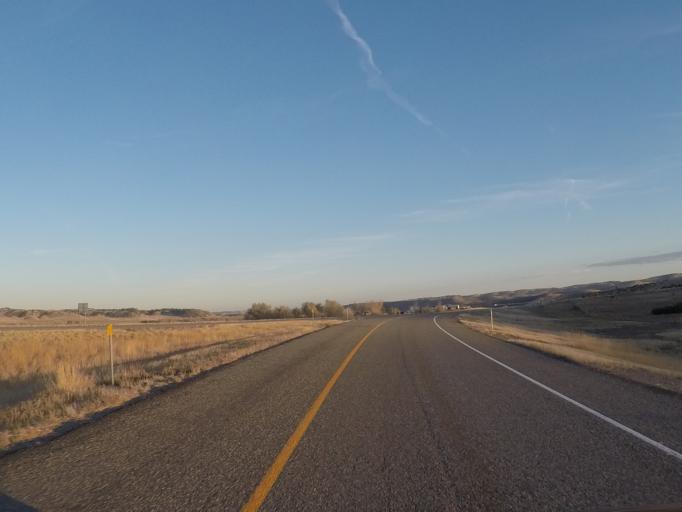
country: US
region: Montana
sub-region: Sweet Grass County
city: Big Timber
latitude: 45.7676
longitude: -109.7929
